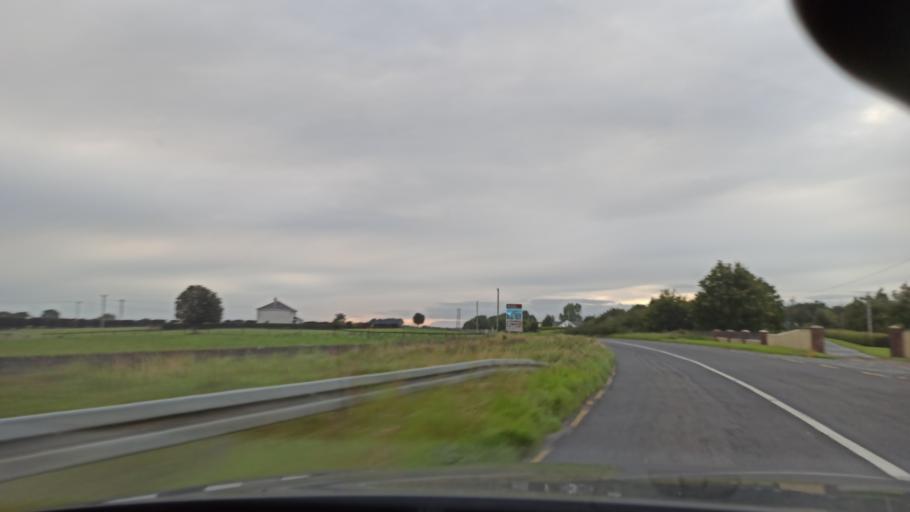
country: IE
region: Munster
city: Cashel
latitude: 52.5003
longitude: -7.8699
